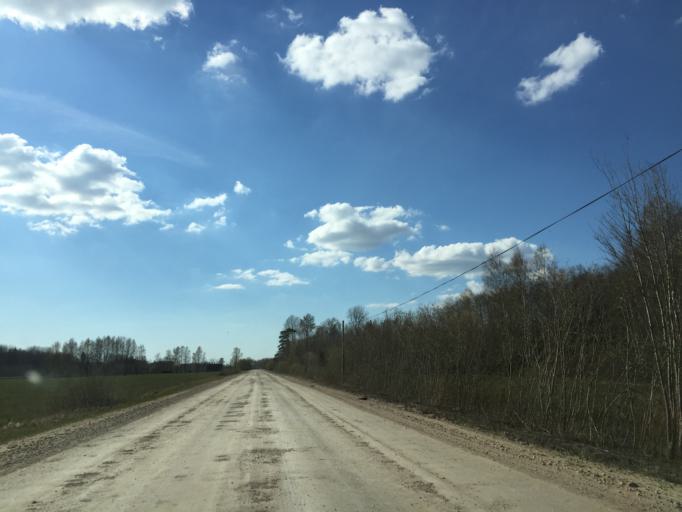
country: LV
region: Krimulda
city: Ragana
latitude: 57.3421
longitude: 24.6110
